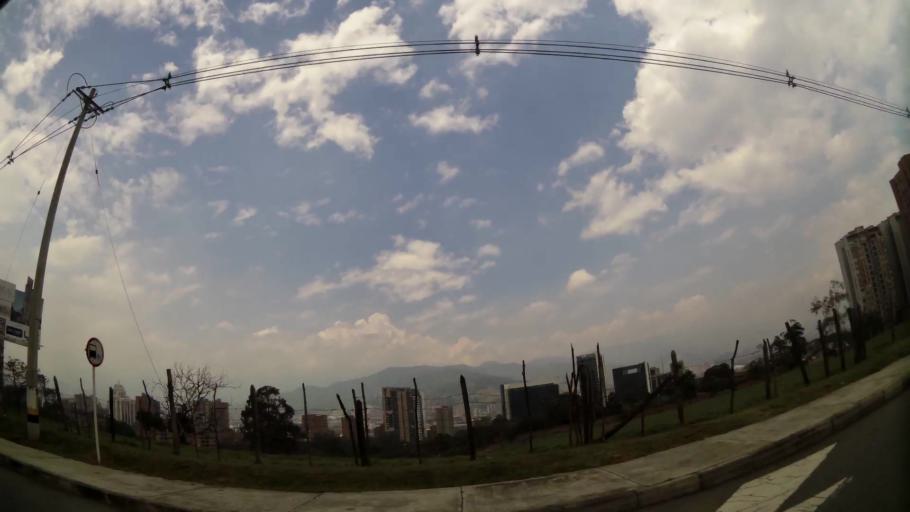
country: CO
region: Antioquia
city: Envigado
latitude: 6.1929
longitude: -75.5720
